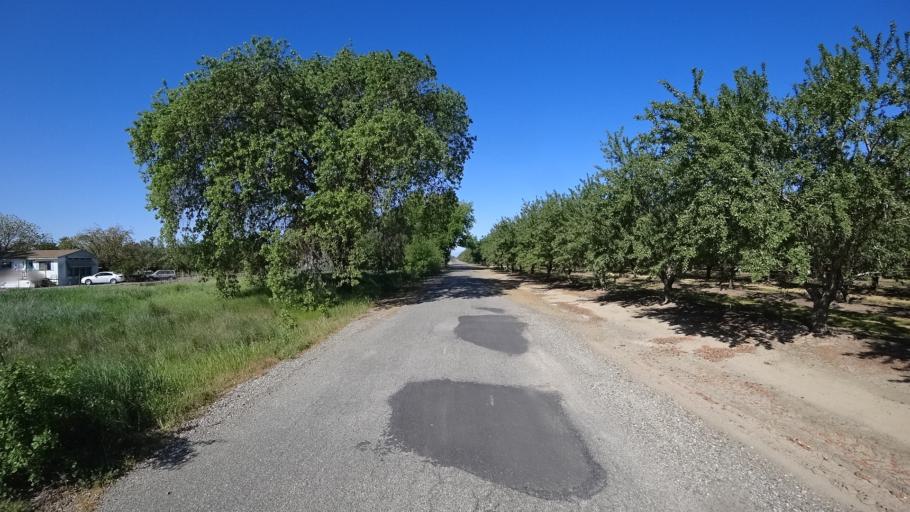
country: US
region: California
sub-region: Glenn County
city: Hamilton City
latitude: 39.7129
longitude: -121.9916
